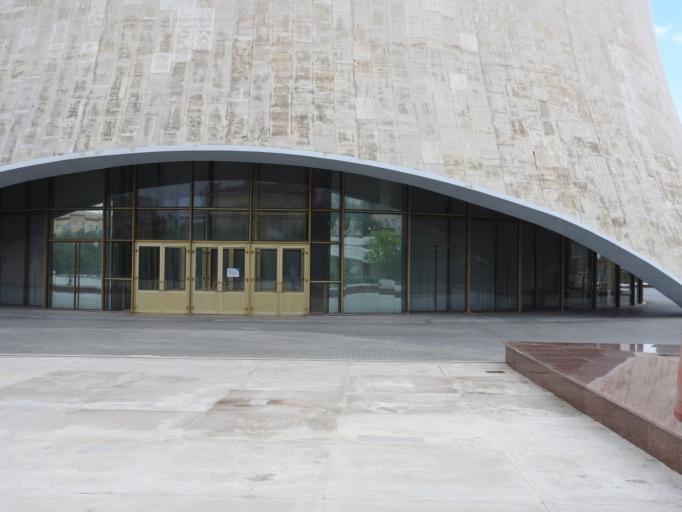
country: RU
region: Volgograd
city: Volgograd
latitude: 48.7152
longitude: 44.5323
